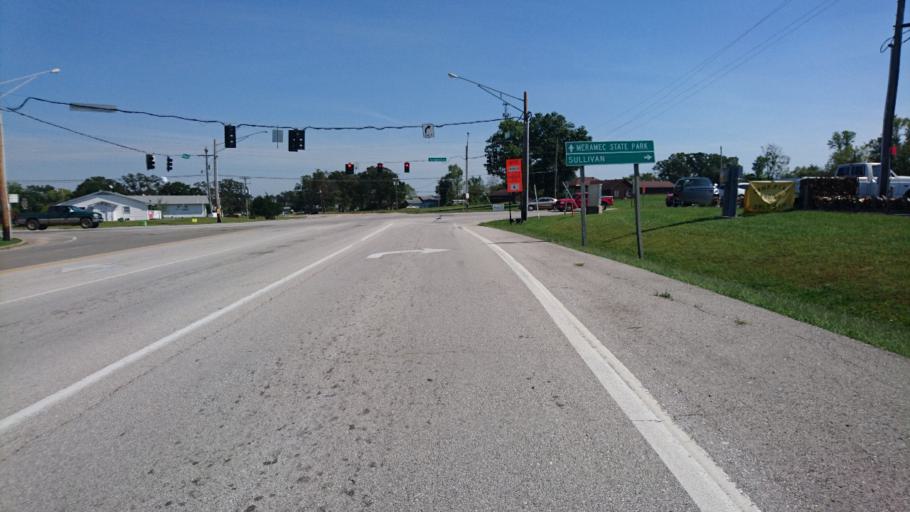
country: US
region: Missouri
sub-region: Franklin County
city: Sullivan
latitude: 38.2229
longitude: -91.1530
